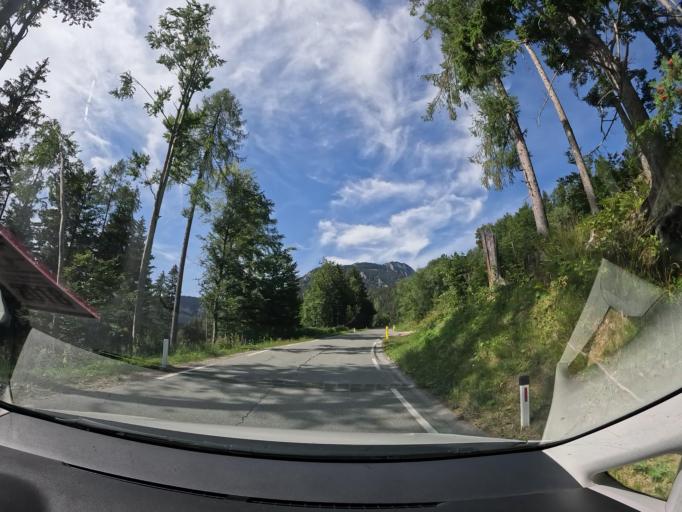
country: AT
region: Carinthia
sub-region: Politischer Bezirk Sankt Veit an der Glan
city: Liebenfels
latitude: 46.7187
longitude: 14.2524
